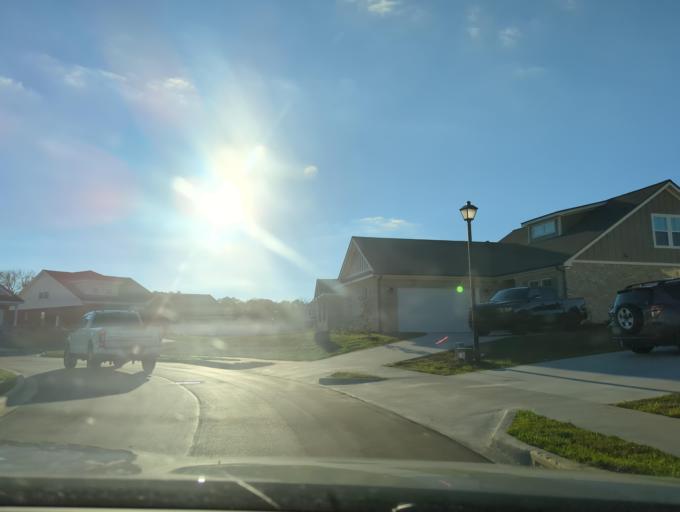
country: US
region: Florida
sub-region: Gadsden County
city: Midway
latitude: 30.5185
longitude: -84.3518
